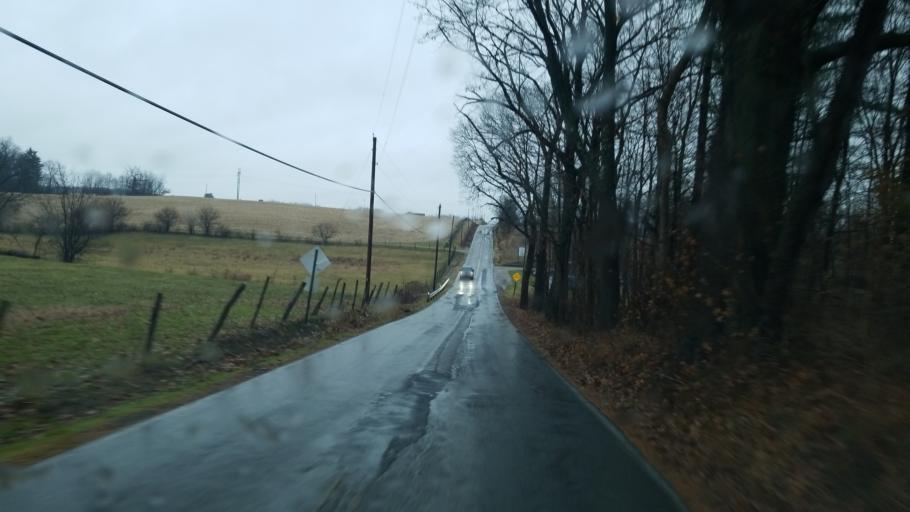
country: US
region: Ohio
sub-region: Licking County
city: Newark
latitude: 40.0747
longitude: -82.3638
